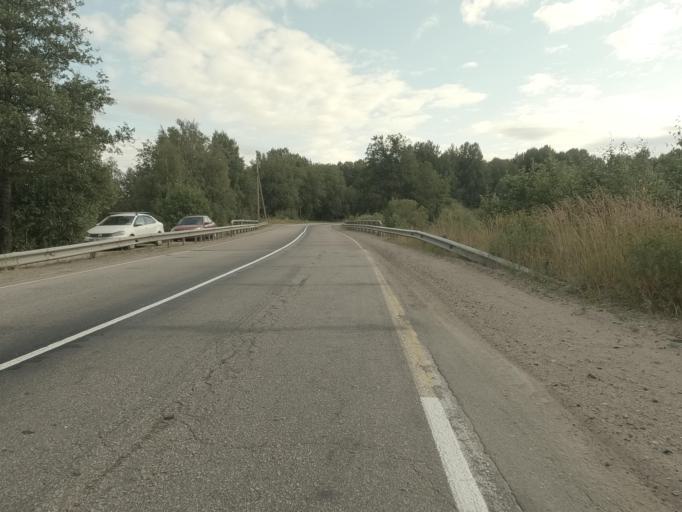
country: RU
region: Leningrad
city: Kamennogorsk
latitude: 60.8685
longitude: 28.9783
